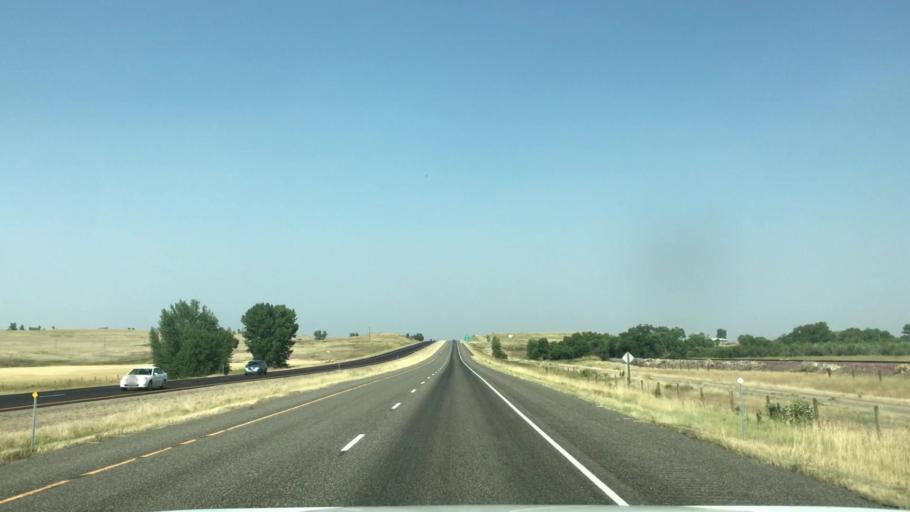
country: US
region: Montana
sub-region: Cascade County
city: Sun Prairie
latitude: 47.2423
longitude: -111.7265
